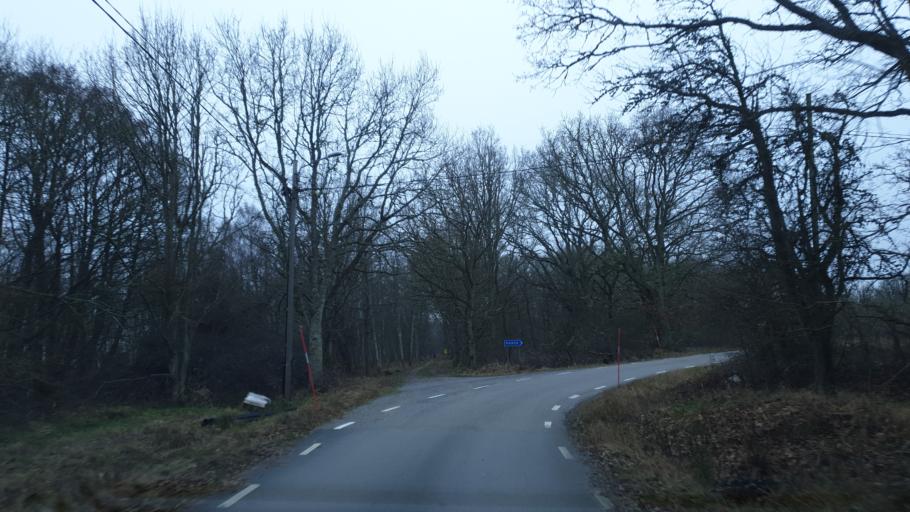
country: SE
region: Blekinge
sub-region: Karlskrona Kommun
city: Karlskrona
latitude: 56.1055
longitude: 15.6105
